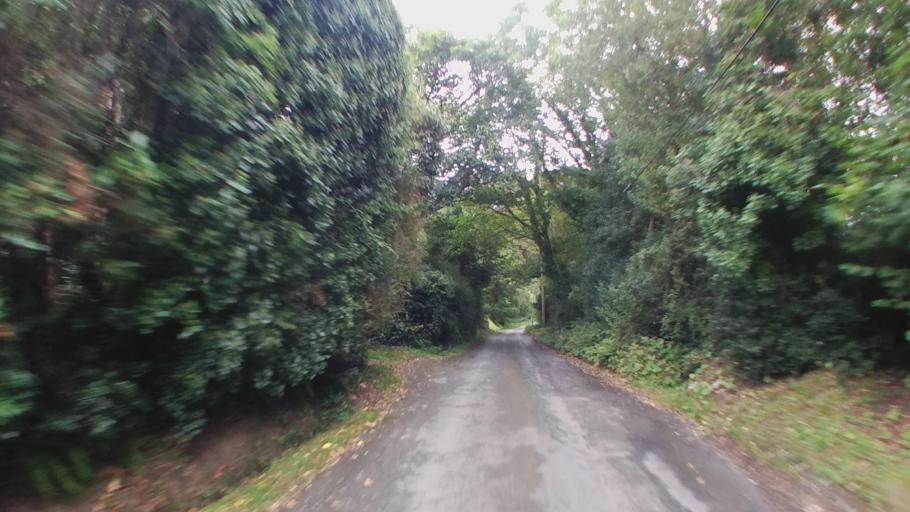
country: IE
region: Leinster
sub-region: Wicklow
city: Enniskerry
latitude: 53.1806
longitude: -6.2101
